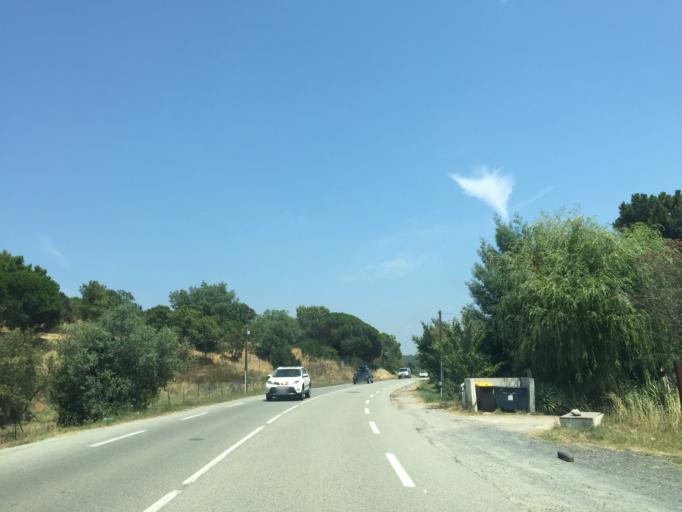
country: FR
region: Provence-Alpes-Cote d'Azur
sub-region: Departement du Var
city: Puget-sur-Argens
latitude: 43.4034
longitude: 6.6811
